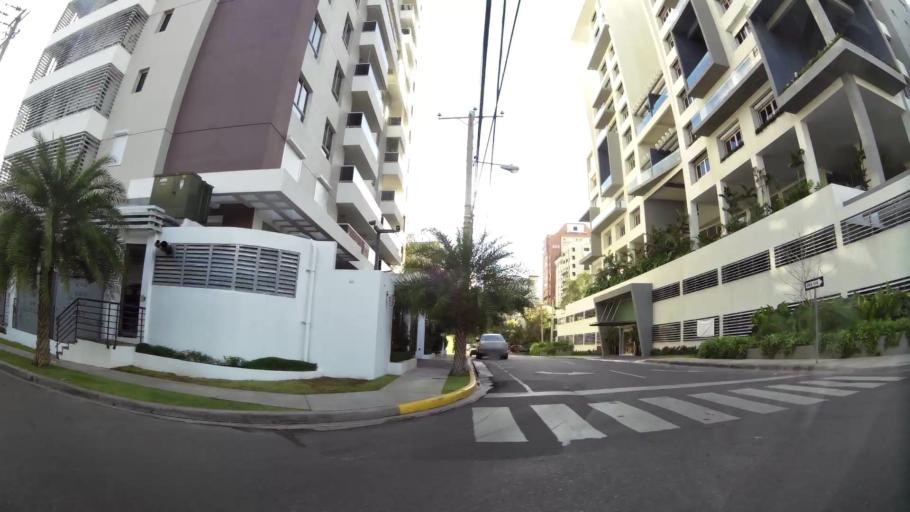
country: DO
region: Nacional
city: La Julia
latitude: 18.4767
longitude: -69.9414
